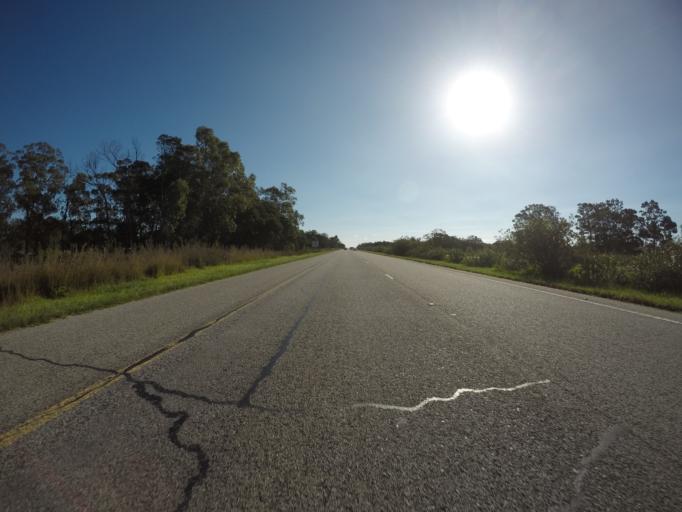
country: ZA
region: Eastern Cape
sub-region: Nelson Mandela Bay Metropolitan Municipality
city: Port Elizabeth
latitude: -33.9444
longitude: 25.3945
